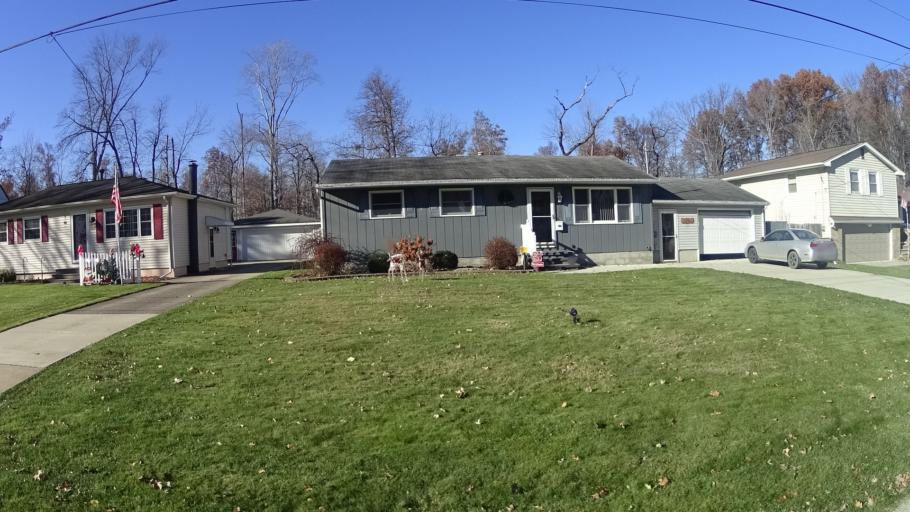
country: US
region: Ohio
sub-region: Lorain County
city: Elyria
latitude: 41.3968
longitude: -82.1563
